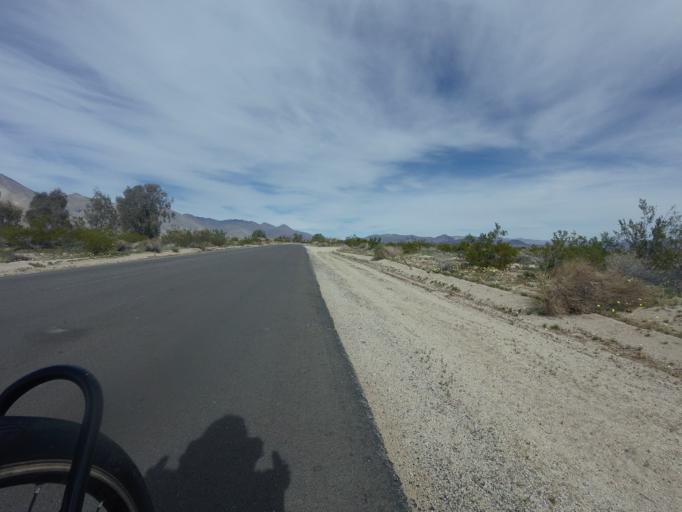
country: US
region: California
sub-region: Kern County
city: Inyokern
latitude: 35.7723
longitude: -117.8498
